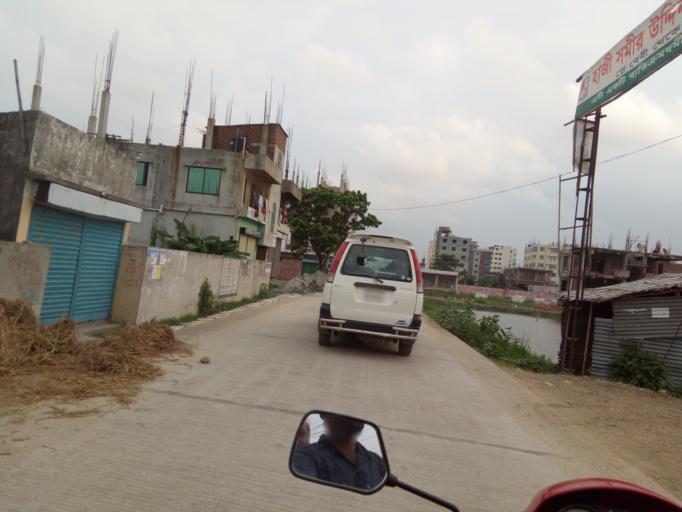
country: BD
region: Dhaka
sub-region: Dhaka
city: Dhaka
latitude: 23.6976
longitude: 90.4752
